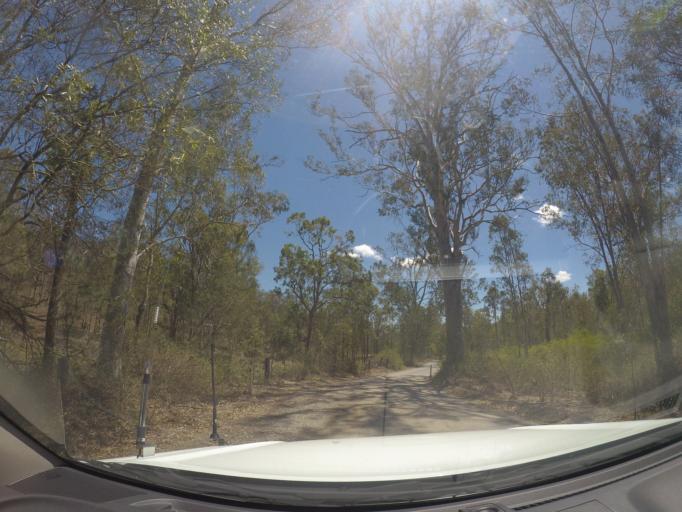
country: AU
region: Queensland
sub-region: Ipswich
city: Redbank Plains
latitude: -27.7572
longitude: 152.8363
